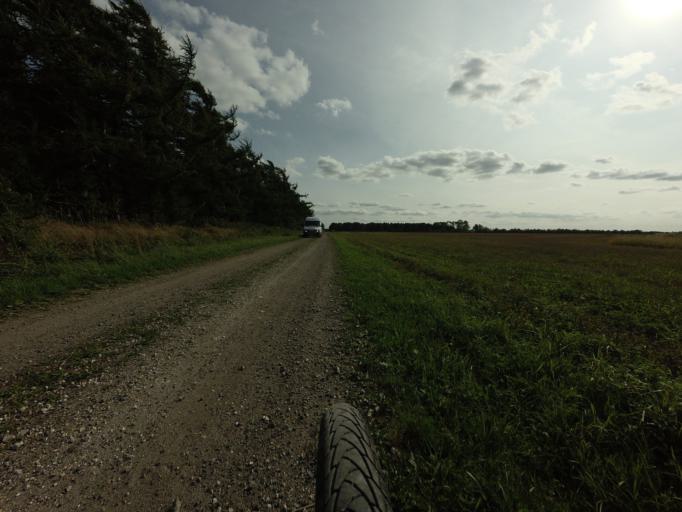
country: DK
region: Zealand
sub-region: Vordingborg Kommune
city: Praesto
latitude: 55.1456
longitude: 12.0911
